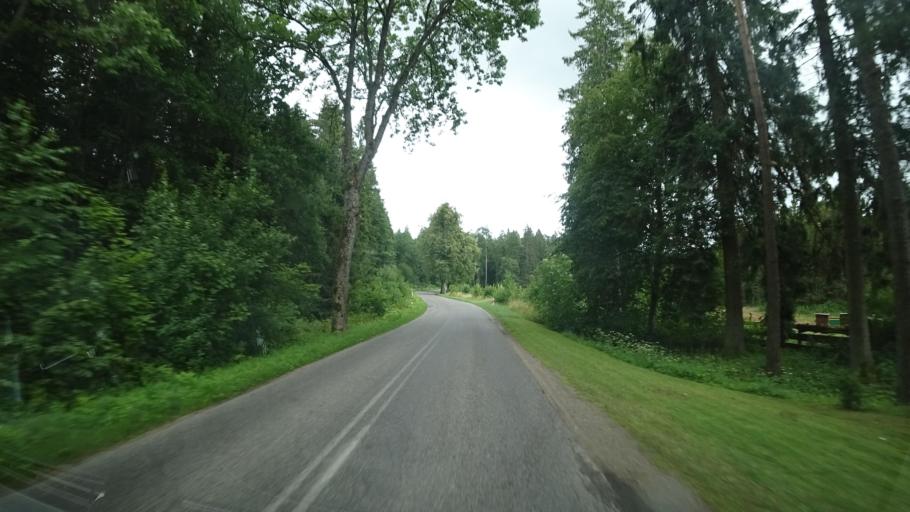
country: PL
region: Warmian-Masurian Voivodeship
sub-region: Powiat goldapski
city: Goldap
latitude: 54.3090
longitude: 22.3948
